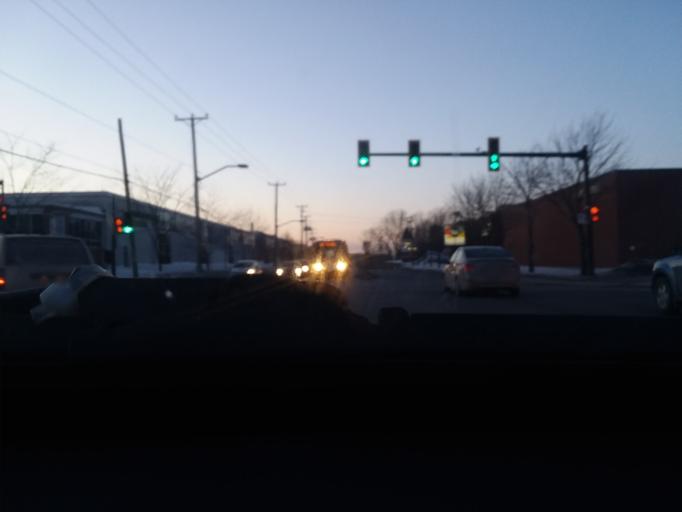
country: CA
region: Quebec
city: Montreal-Ouest
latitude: 45.4375
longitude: -73.6424
